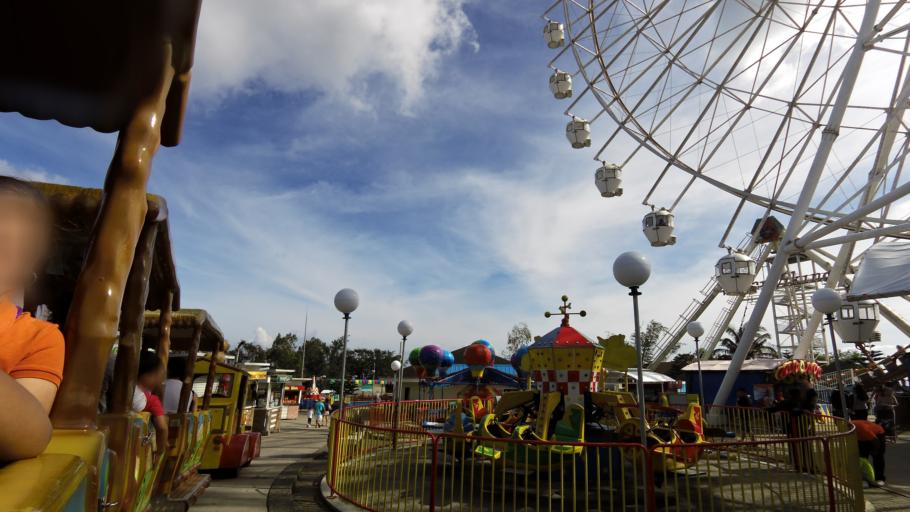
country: PH
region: Calabarzon
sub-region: Province of Batangas
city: Sampaloc
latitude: 14.0950
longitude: 120.9385
